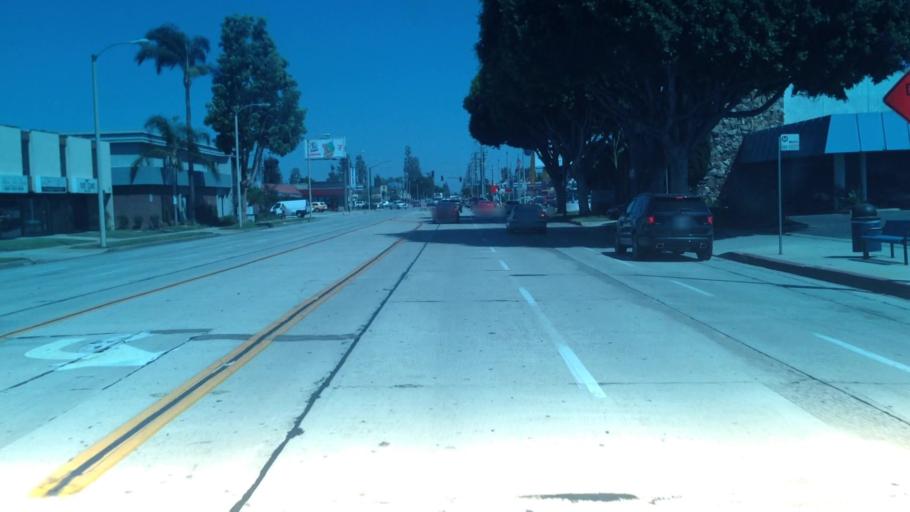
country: US
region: California
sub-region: Los Angeles County
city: Downey
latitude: 33.9486
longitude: -118.1194
